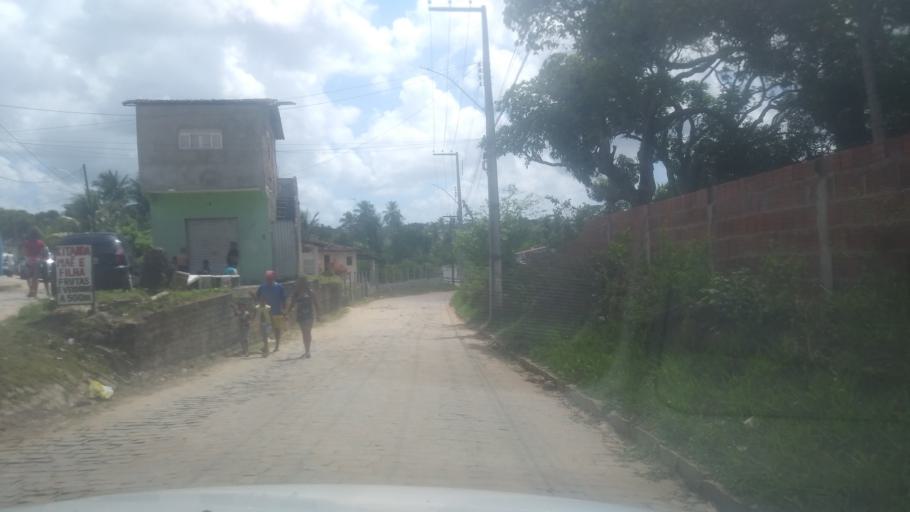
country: BR
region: Rio Grande do Norte
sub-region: Sao Jose De Mipibu
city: Sao Jose de Mipibu
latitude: -6.0721
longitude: -35.2304
